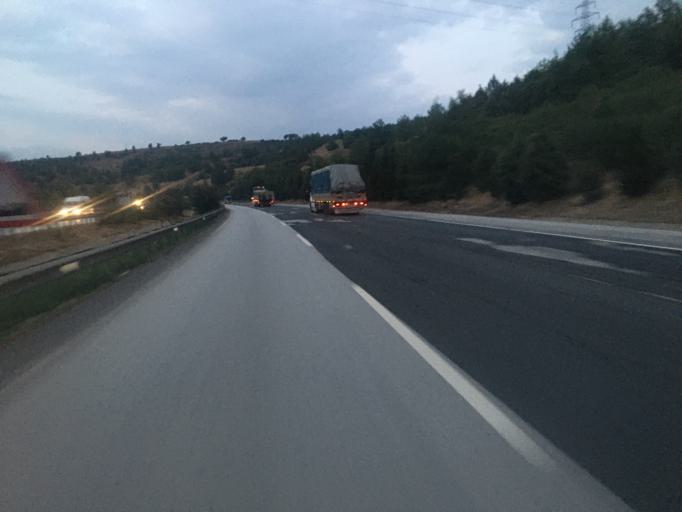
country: TR
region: Osmaniye
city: Haruniye
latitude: 37.1770
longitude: 36.3778
